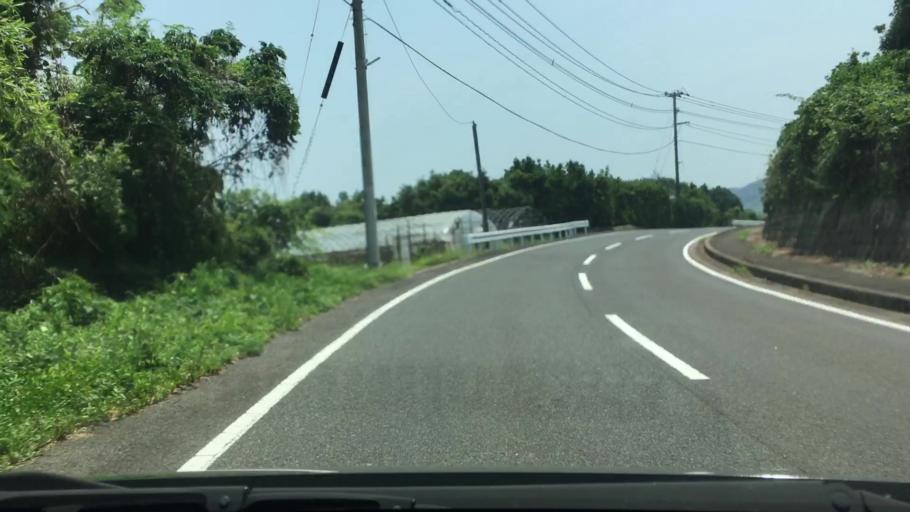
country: JP
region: Nagasaki
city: Sasebo
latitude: 33.0691
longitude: 129.6804
